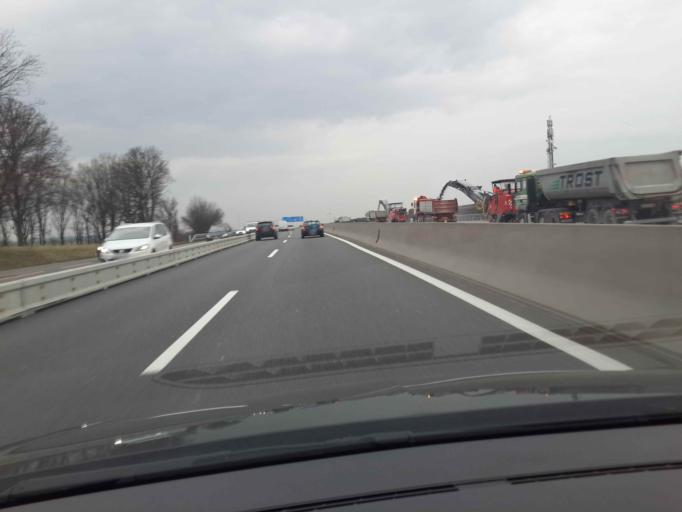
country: AT
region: Lower Austria
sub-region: Politischer Bezirk Sankt Polten
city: Pyhra
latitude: 48.1861
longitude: 15.6895
